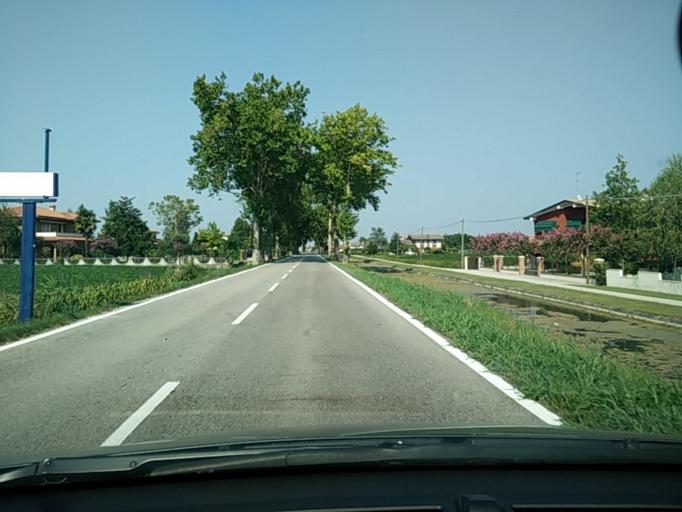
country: IT
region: Veneto
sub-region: Provincia di Venezia
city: Crepaldo
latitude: 45.6096
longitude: 12.7109
